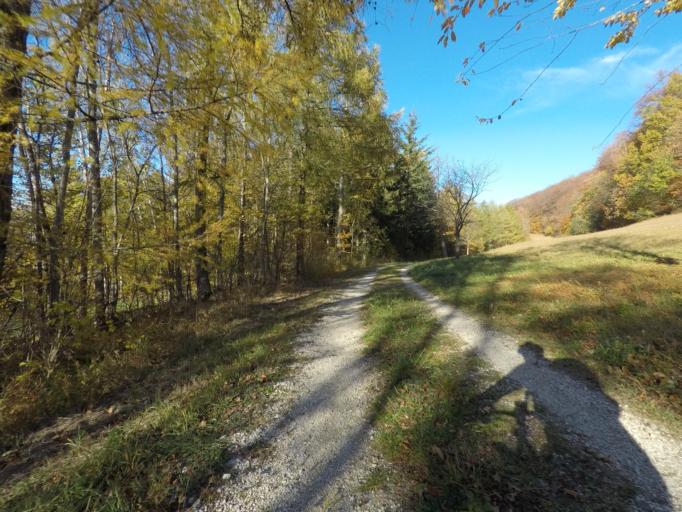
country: DE
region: Baden-Wuerttemberg
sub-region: Tuebingen Region
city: Pfullingen
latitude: 48.4395
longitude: 9.2215
